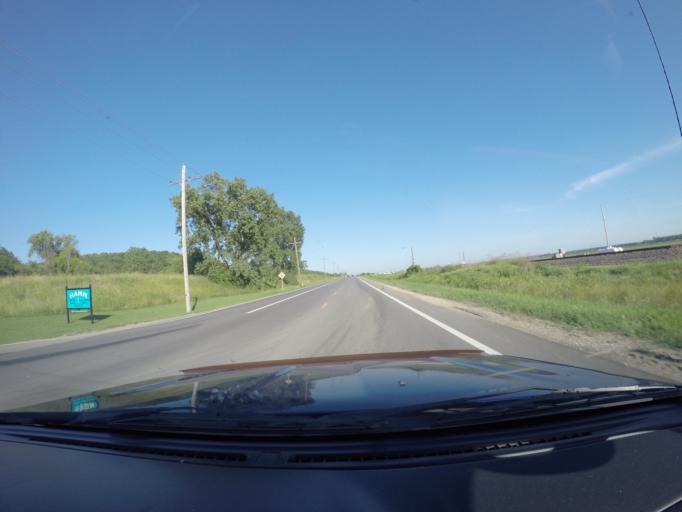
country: US
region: Kansas
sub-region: Douglas County
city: Lawrence
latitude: 39.0436
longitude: -95.2691
